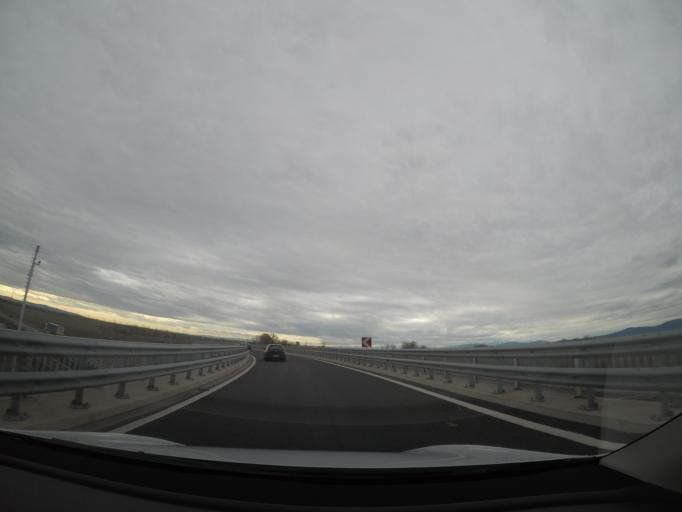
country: AT
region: Lower Austria
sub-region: Politischer Bezirk Modling
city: Munchendorf
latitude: 48.0216
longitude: 16.3551
